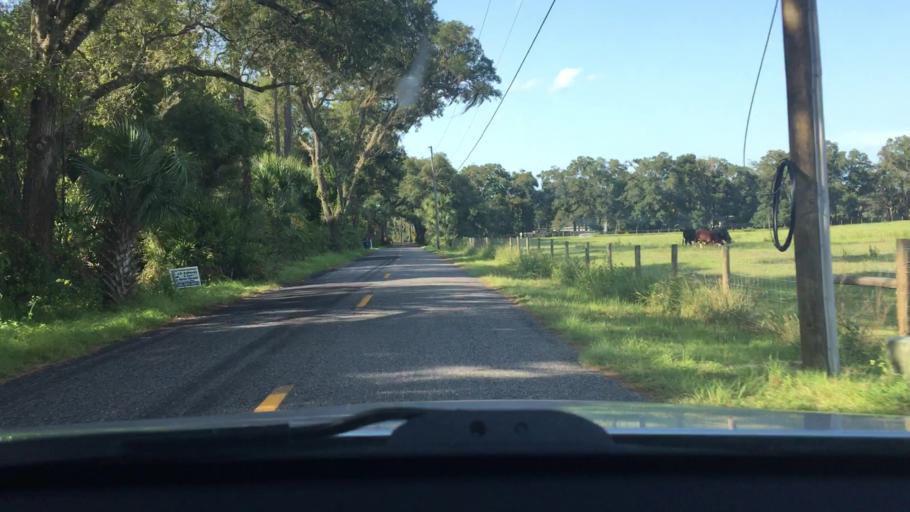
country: US
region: Florida
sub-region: Volusia County
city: Lake Helen
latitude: 28.9679
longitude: -81.2151
